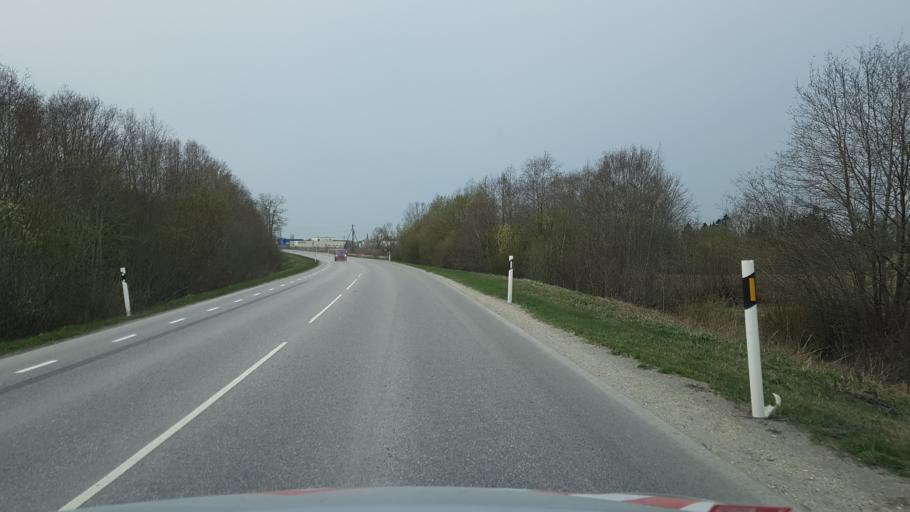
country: EE
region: Harju
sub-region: Joelaehtme vald
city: Loo
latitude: 59.4115
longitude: 24.9266
